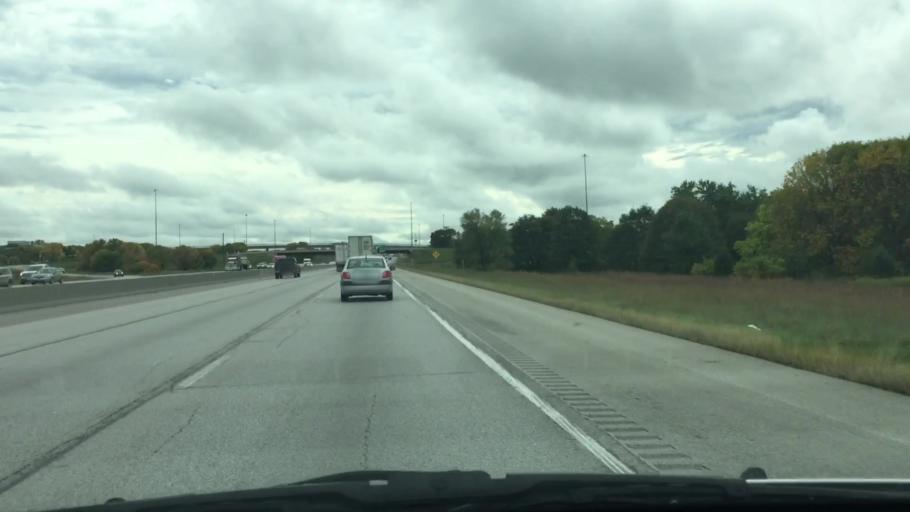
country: US
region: Iowa
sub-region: Polk County
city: Clive
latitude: 41.6042
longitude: -93.7737
